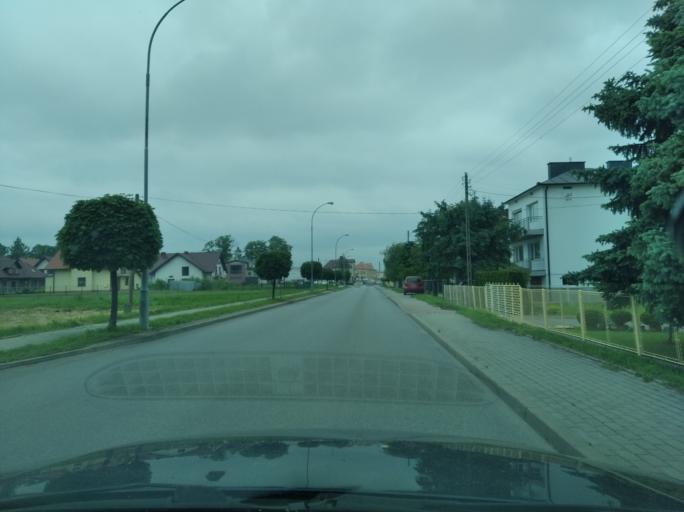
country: PL
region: Subcarpathian Voivodeship
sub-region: Powiat ropczycko-sedziszowski
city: Sedziszow Malopolski
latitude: 50.0671
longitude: 21.6894
